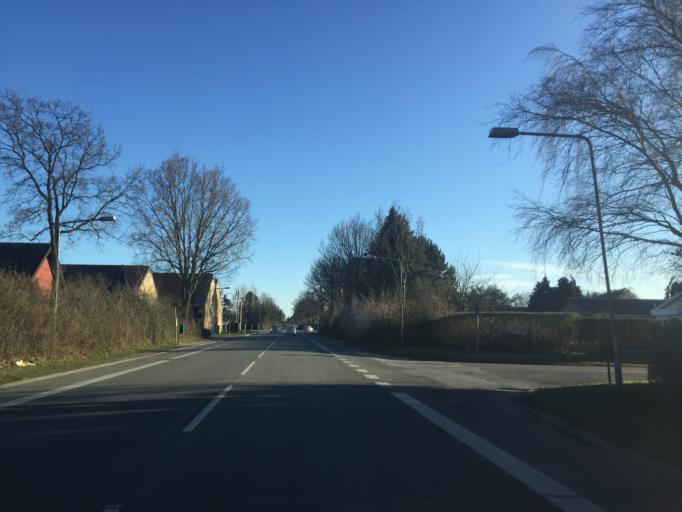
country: DK
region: Capital Region
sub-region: Dragor Kommune
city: Dragor
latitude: 55.5965
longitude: 12.6582
